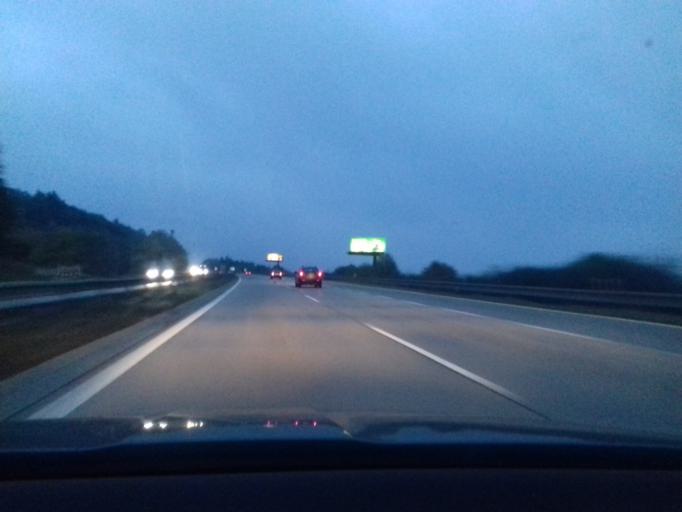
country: CZ
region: Vysocina
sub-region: Okres Zd'ar nad Sazavou
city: Velke Mezirici
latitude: 49.3659
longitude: 15.9844
